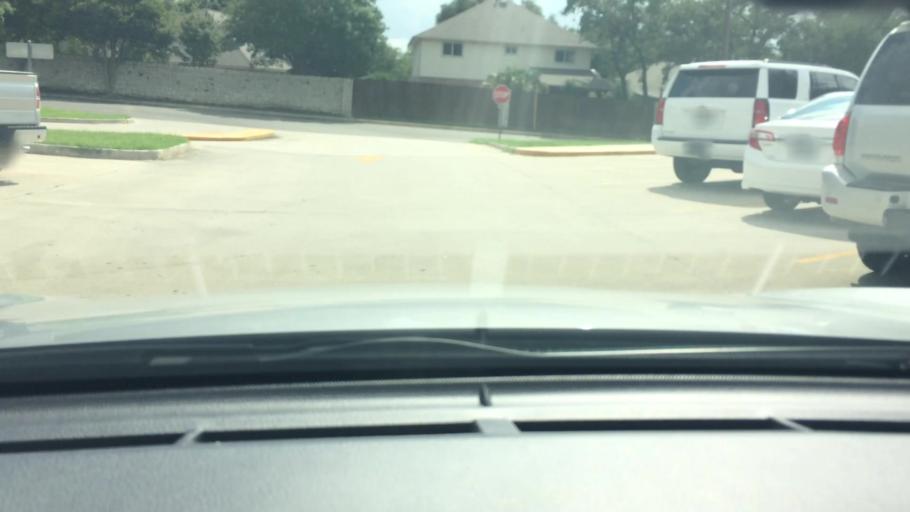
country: US
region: Texas
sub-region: Bexar County
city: Shavano Park
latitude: 29.5624
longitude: -98.5611
